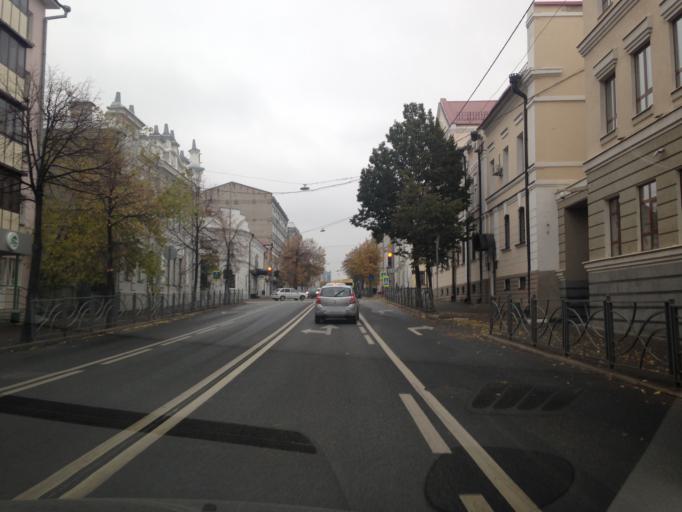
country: RU
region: Tatarstan
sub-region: Gorod Kazan'
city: Kazan
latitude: 55.7966
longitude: 49.1207
